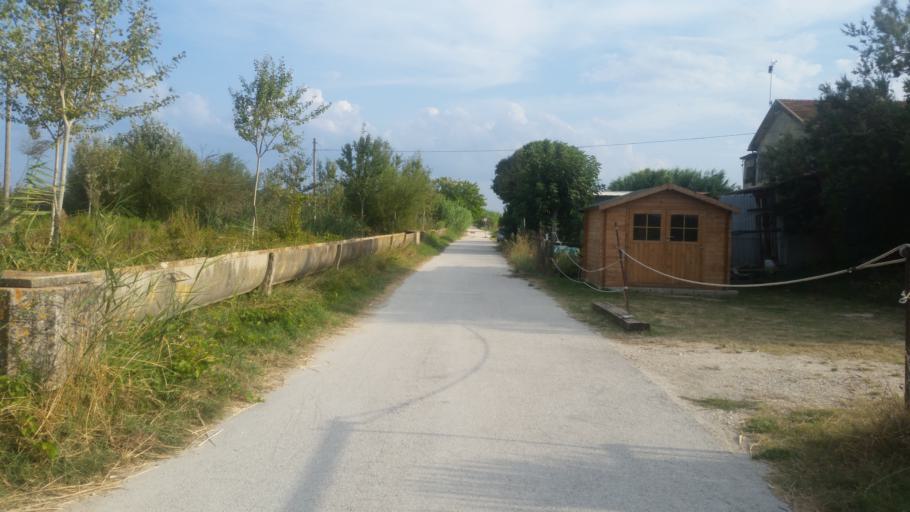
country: IT
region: Abruzzo
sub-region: Provincia di Teramo
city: Martinsicuro
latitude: 42.9041
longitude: 13.9072
